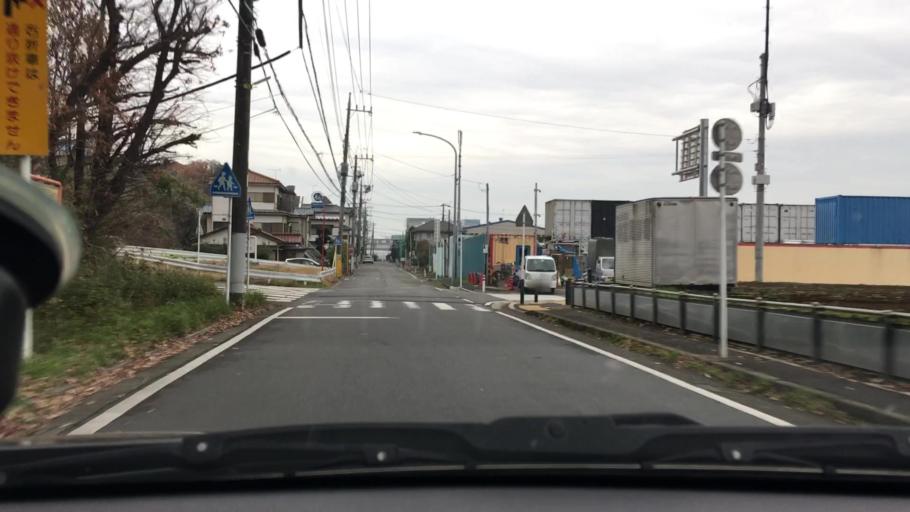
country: JP
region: Kanagawa
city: Yokohama
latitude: 35.5195
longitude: 139.6040
